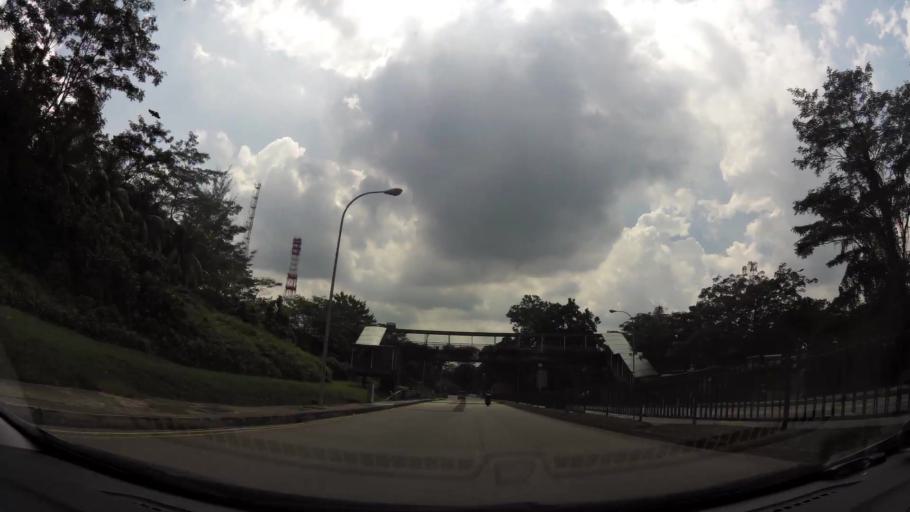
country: MY
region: Johor
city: Johor Bahru
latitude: 1.4336
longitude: 103.7620
